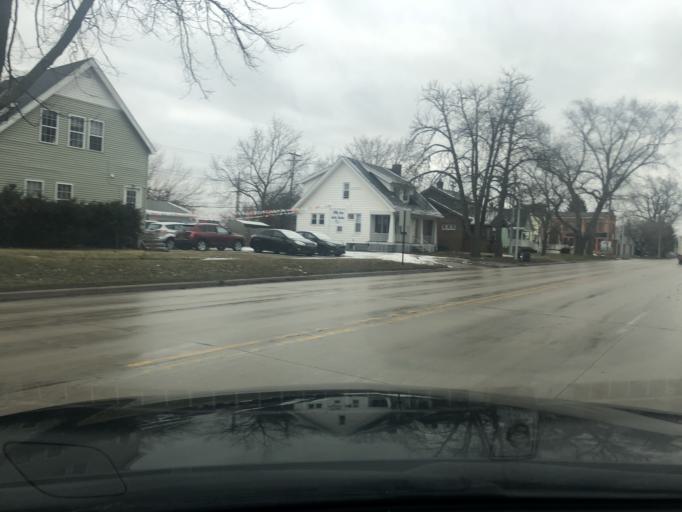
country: US
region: Michigan
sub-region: Saint Clair County
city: Port Huron
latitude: 42.9932
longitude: -82.4343
